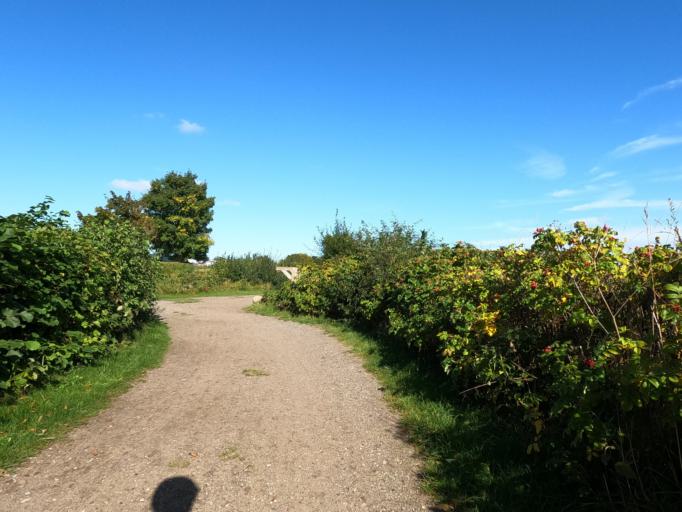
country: DE
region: Schleswig-Holstein
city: Neukirchen
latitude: 54.3044
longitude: 11.0756
